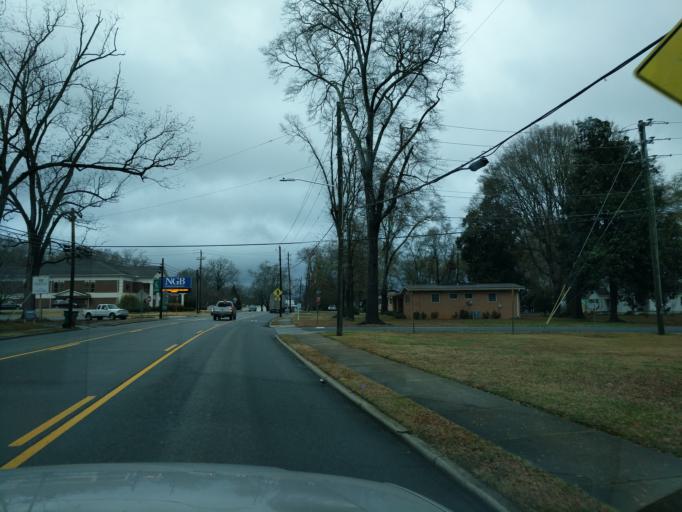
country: US
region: Georgia
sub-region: Franklin County
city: Lavonia
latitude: 34.4302
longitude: -83.1071
